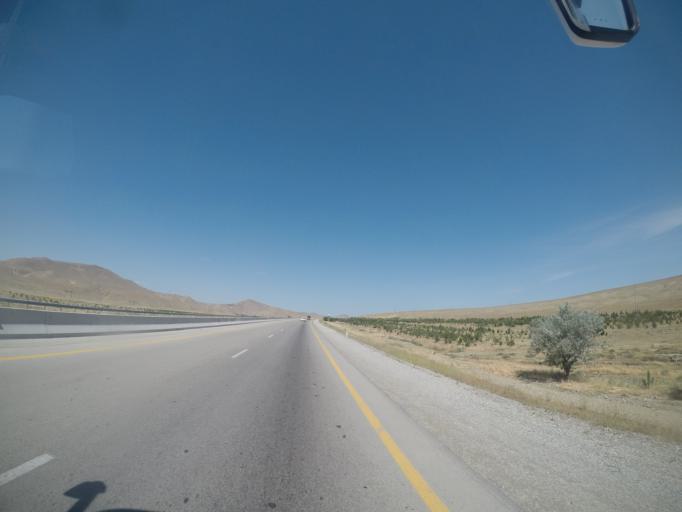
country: AZ
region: Sumqayit
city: Haci Zeynalabdin
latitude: 40.4995
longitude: 49.2924
